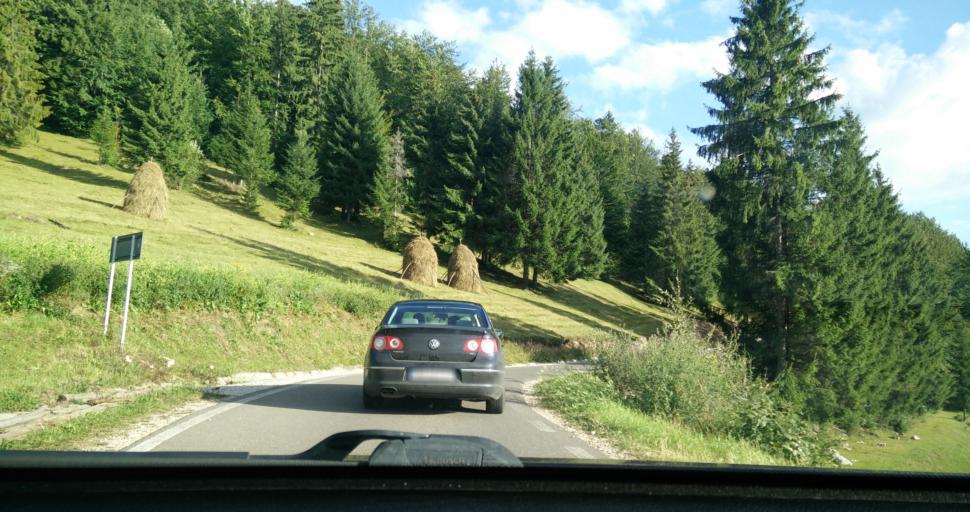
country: RO
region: Alba
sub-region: Comuna Scarisoara
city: Scarisoara
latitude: 46.4798
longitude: 22.8302
